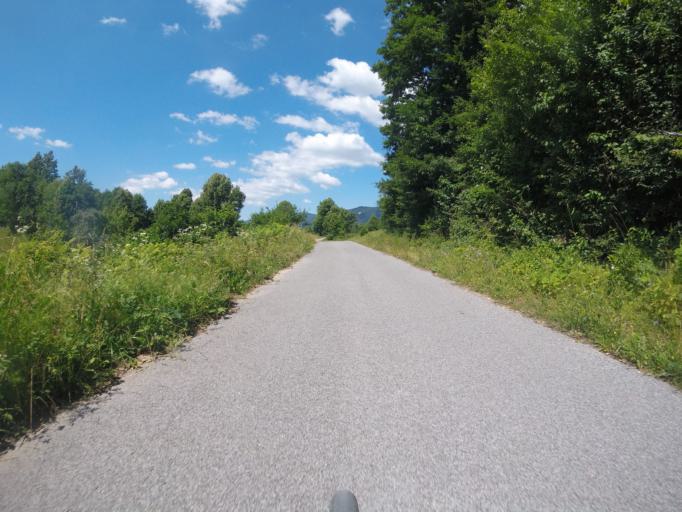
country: SI
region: Kostanjevica na Krki
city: Kostanjevica na Krki
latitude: 45.7616
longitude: 15.4373
